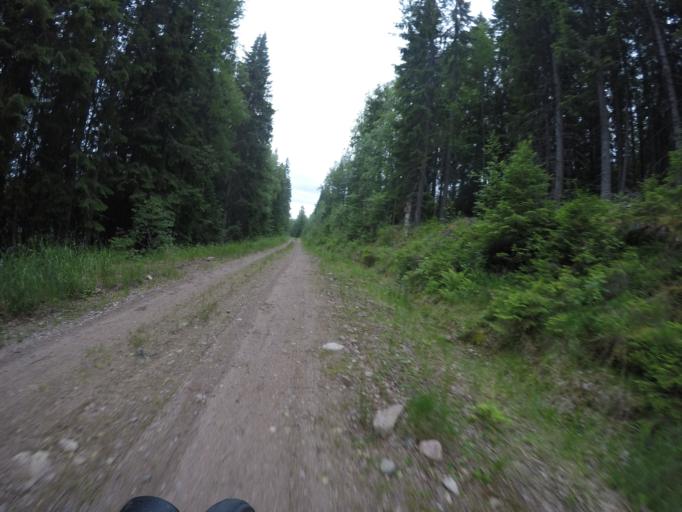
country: SE
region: Dalarna
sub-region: Ludvika Kommun
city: Abborrberget
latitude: 60.0416
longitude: 14.5931
